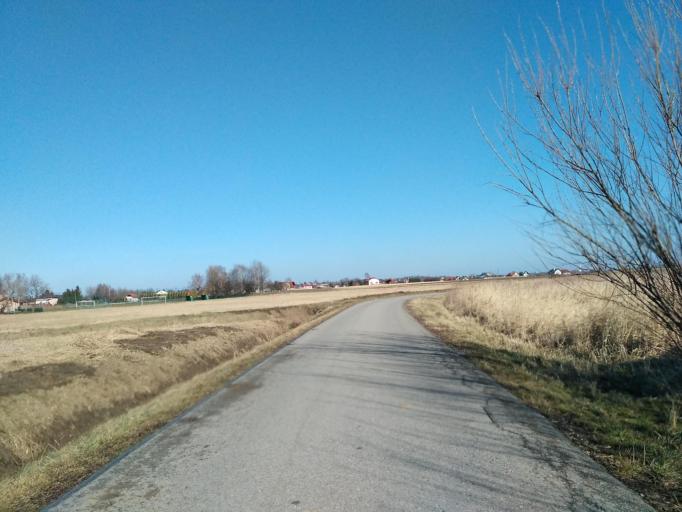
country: PL
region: Subcarpathian Voivodeship
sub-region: Powiat rzeszowski
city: Lutoryz
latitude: 49.9587
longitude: 21.9268
